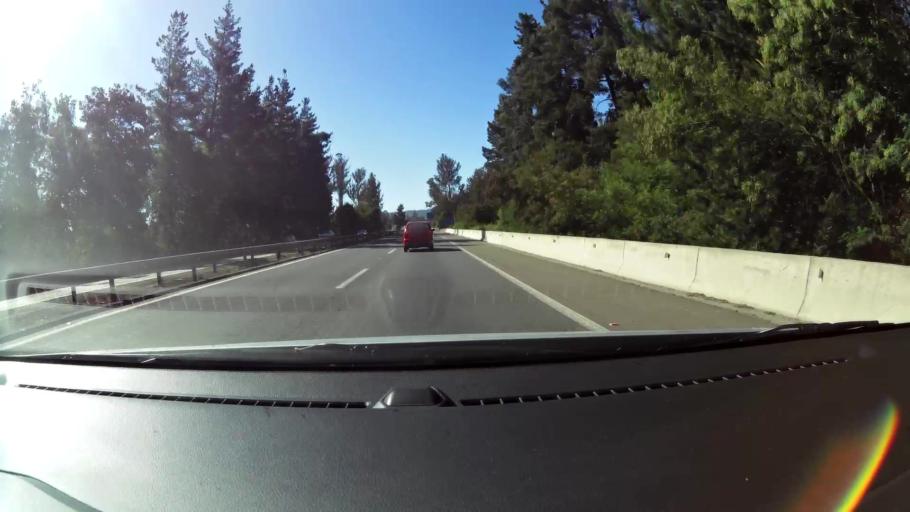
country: CL
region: Valparaiso
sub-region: Provincia de Valparaiso
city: Vina del Mar
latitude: -33.1505
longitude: -71.5580
